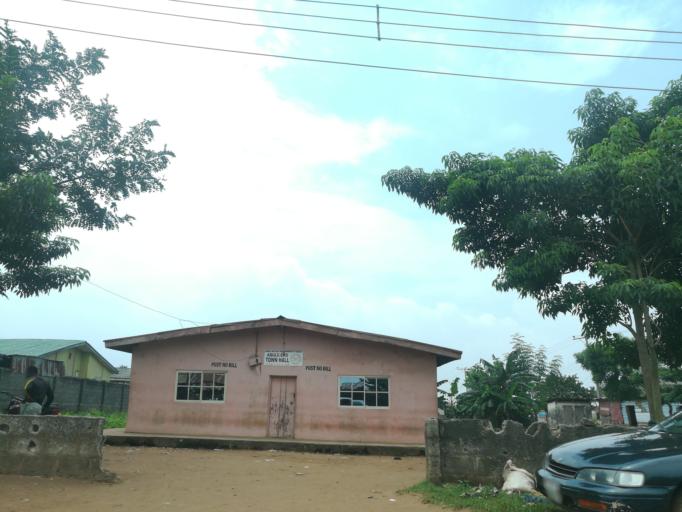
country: NG
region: Lagos
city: Ikorodu
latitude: 6.5827
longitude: 3.5928
